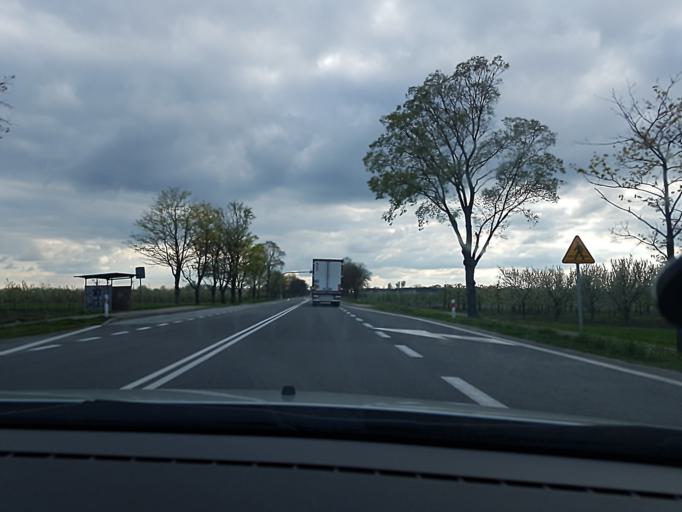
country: PL
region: Lodz Voivodeship
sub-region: powiat Lowicki
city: Nieborow
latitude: 52.1375
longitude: 20.0587
